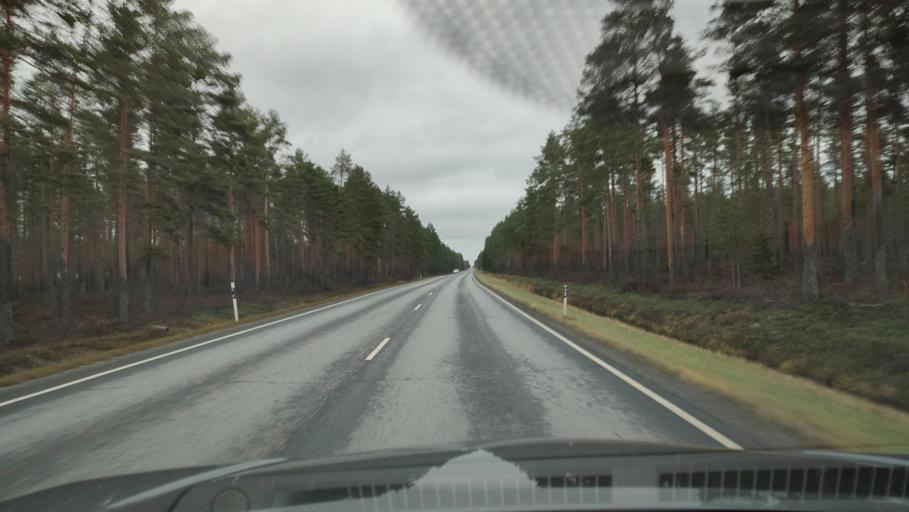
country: FI
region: Southern Ostrobothnia
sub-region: Seinaejoki
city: Kurikka
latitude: 62.5156
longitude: 22.3133
